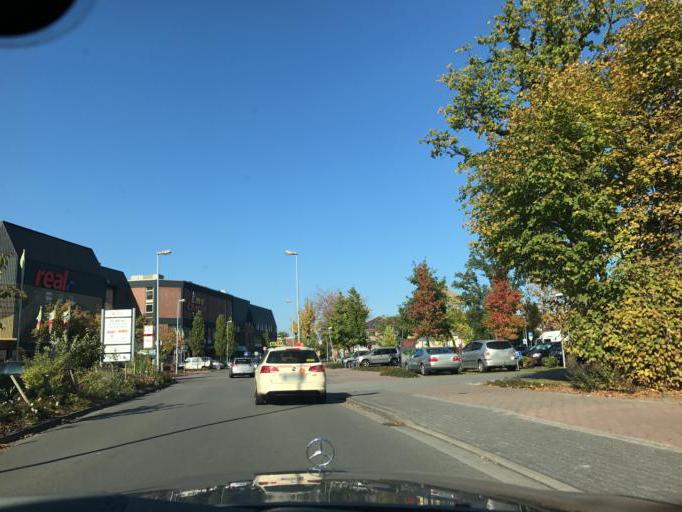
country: DE
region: Lower Saxony
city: Papenburg
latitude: 53.0829
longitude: 7.3886
